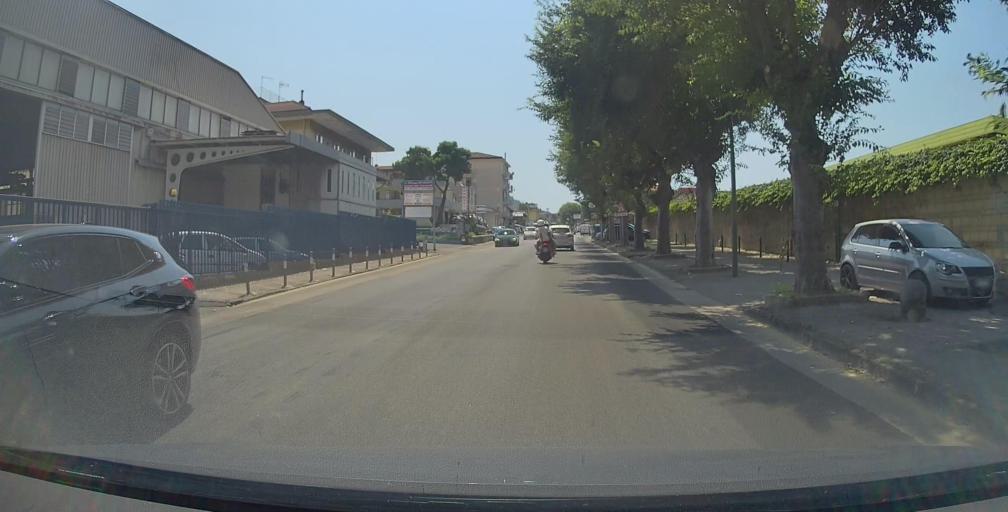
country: IT
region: Campania
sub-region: Provincia di Salerno
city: Cava De Tirreni
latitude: 40.7212
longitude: 14.6968
